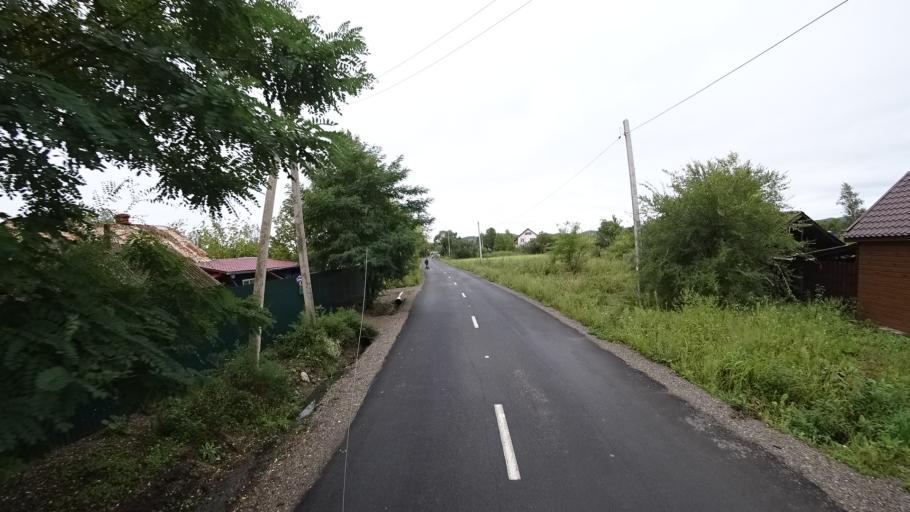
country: RU
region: Primorskiy
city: Monastyrishche
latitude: 44.1980
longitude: 132.4973
